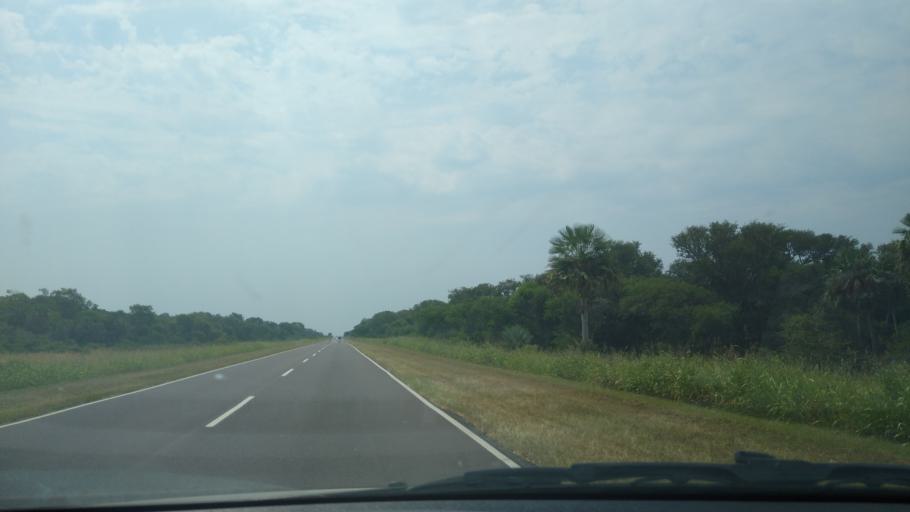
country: AR
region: Chaco
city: La Eduvigis
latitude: -27.0166
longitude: -58.9690
